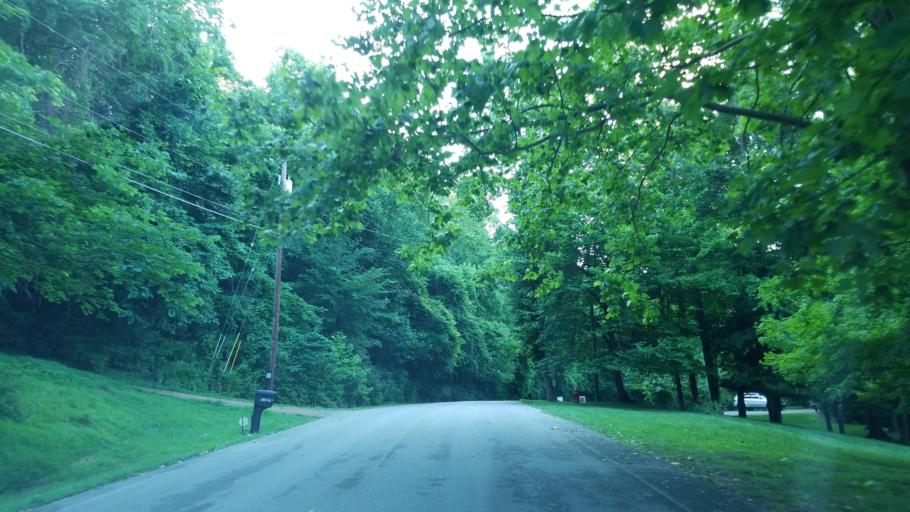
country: US
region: Tennessee
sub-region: Williamson County
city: Brentwood
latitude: 36.0491
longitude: -86.7928
